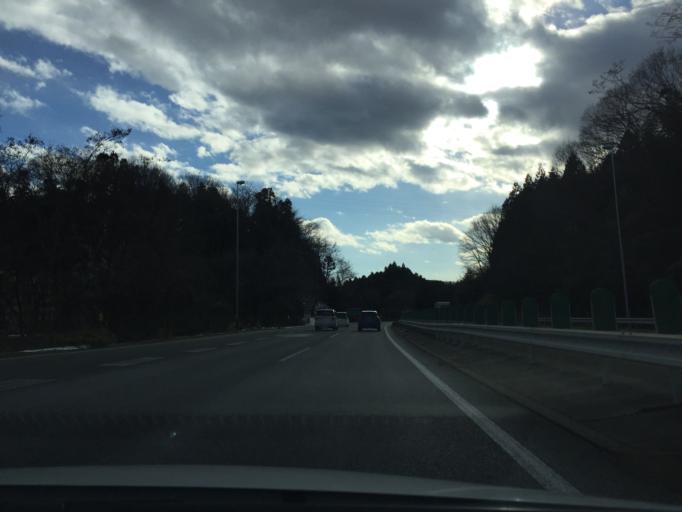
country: JP
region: Fukushima
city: Sukagawa
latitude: 37.1493
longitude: 140.2415
